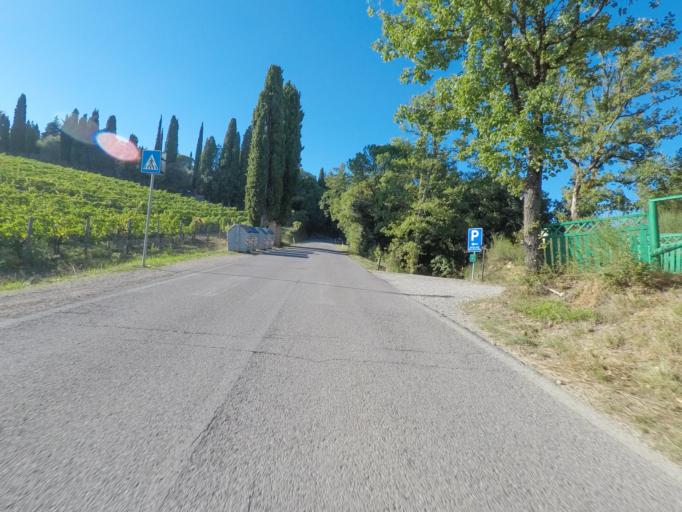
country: IT
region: Tuscany
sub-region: Provincia di Siena
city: Radda in Chianti
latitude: 43.4131
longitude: 11.3513
